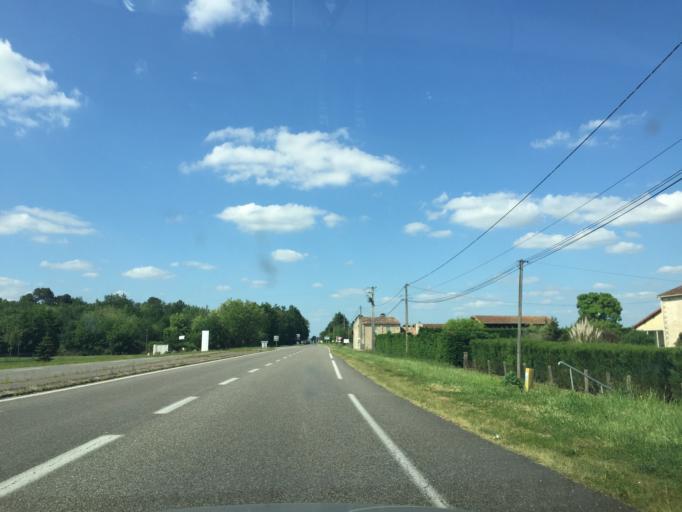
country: FR
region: Aquitaine
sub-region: Departement de la Gironde
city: La Reole
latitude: 44.5130
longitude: -0.0516
